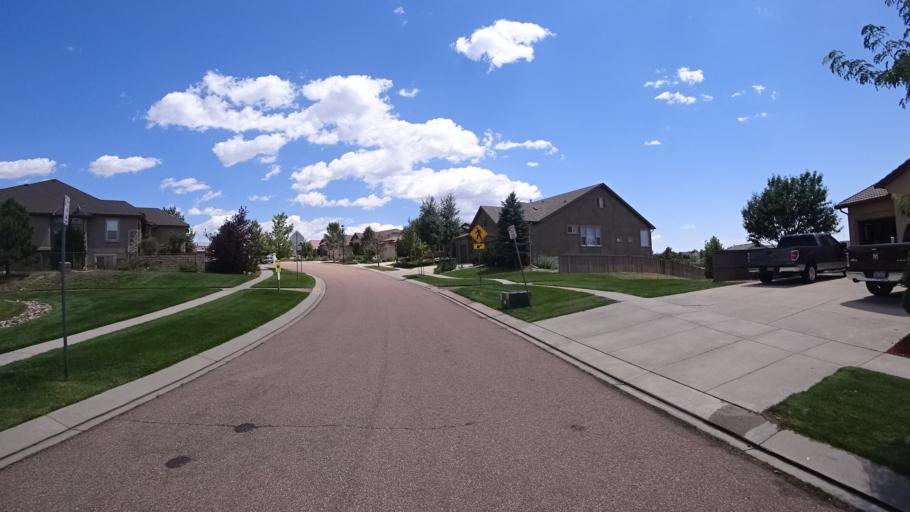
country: US
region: Colorado
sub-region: El Paso County
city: Black Forest
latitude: 38.9685
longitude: -104.7607
